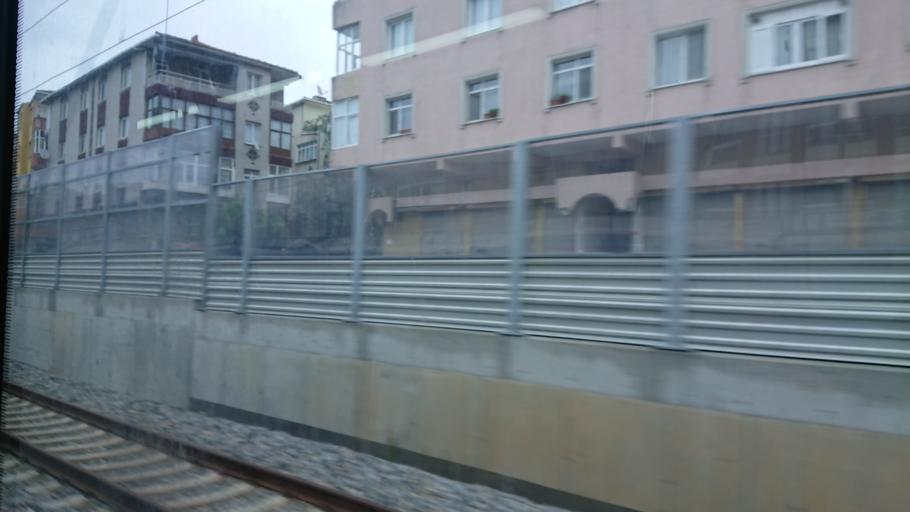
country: TR
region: Istanbul
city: Mahmutbey
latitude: 40.9983
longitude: 28.7675
